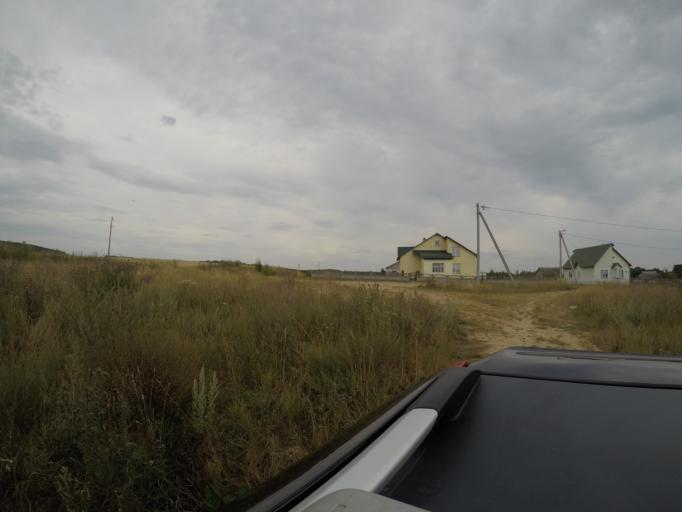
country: BY
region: Grodnenskaya
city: Hal'shany
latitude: 54.2571
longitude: 26.0253
